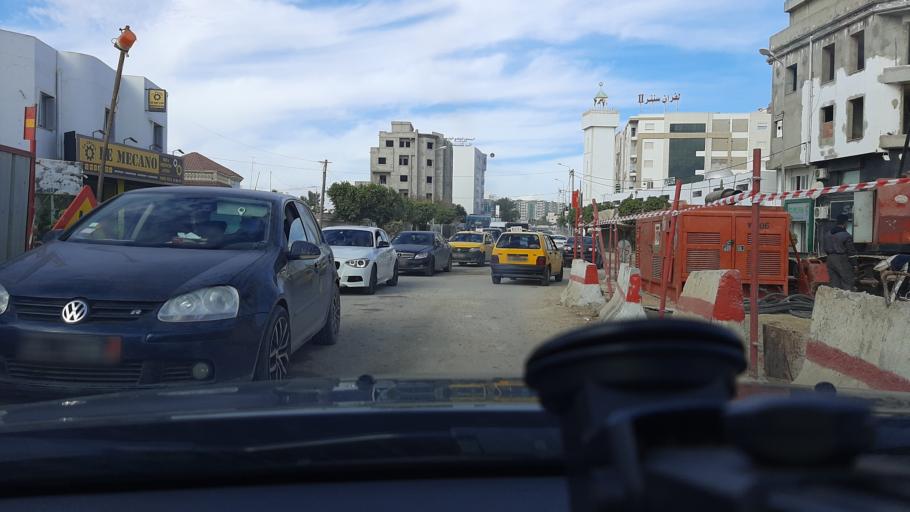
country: TN
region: Safaqis
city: Sfax
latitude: 34.7567
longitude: 10.7348
